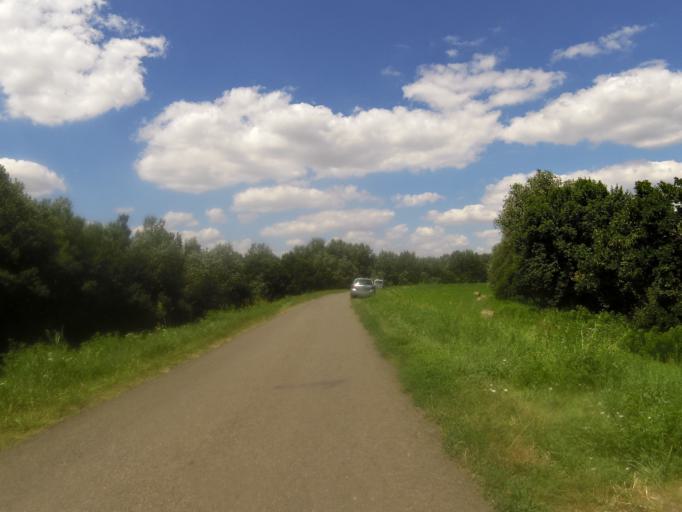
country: HU
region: Heves
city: Tiszanana
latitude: 47.5533
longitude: 20.6044
